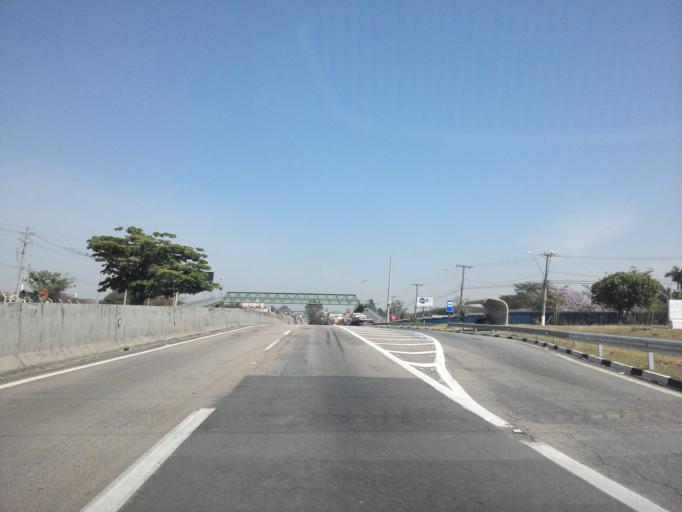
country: BR
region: Sao Paulo
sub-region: Hortolandia
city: Hortolandia
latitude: -22.8964
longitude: -47.1885
